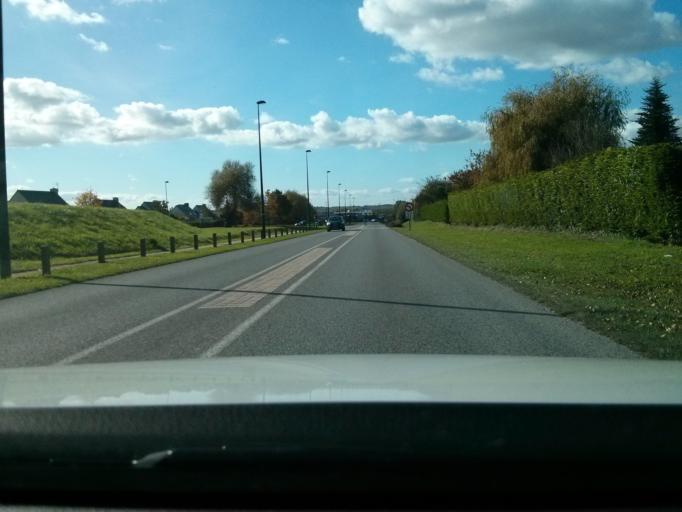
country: FR
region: Brittany
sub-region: Departement des Cotes-d'Armor
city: Ploubalay
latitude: 48.5788
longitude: -2.1460
